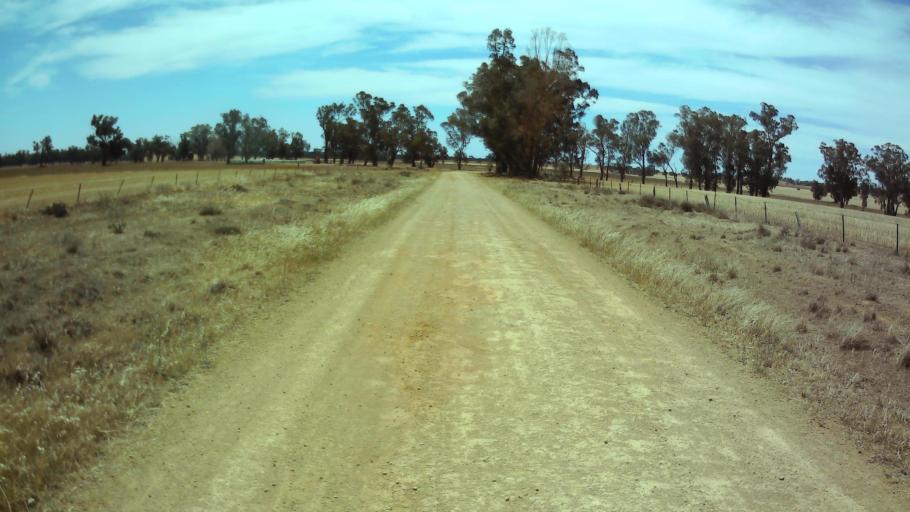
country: AU
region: New South Wales
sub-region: Weddin
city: Grenfell
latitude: -33.7602
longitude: 148.1402
